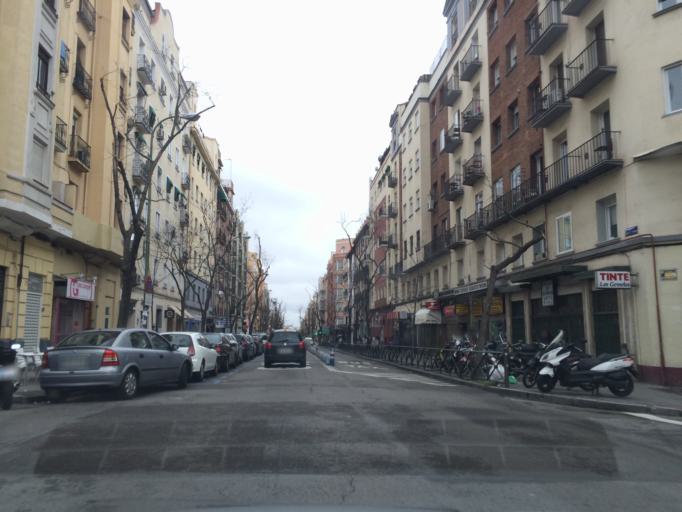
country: ES
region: Madrid
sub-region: Provincia de Madrid
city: Chamberi
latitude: 40.4365
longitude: -3.7131
